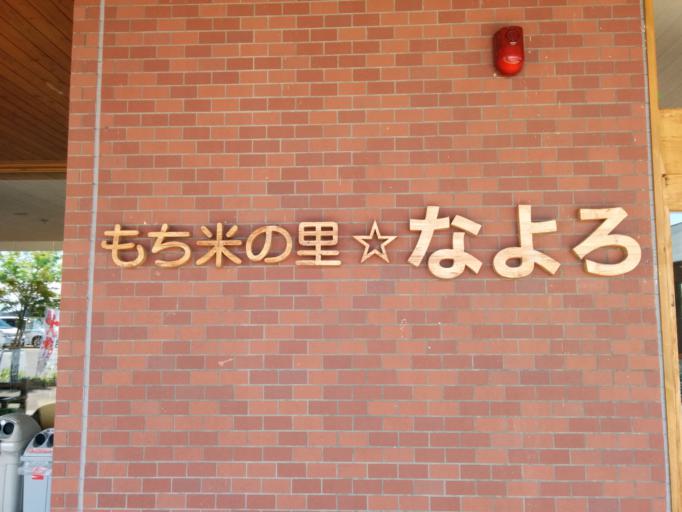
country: JP
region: Hokkaido
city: Nayoro
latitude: 44.2870
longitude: 142.4140
